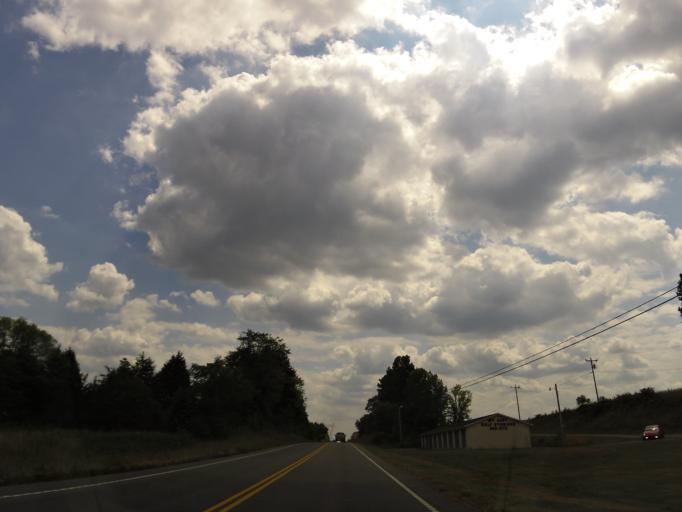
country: US
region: Tennessee
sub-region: Sequatchie County
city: Dunlap
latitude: 35.4377
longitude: -85.3485
